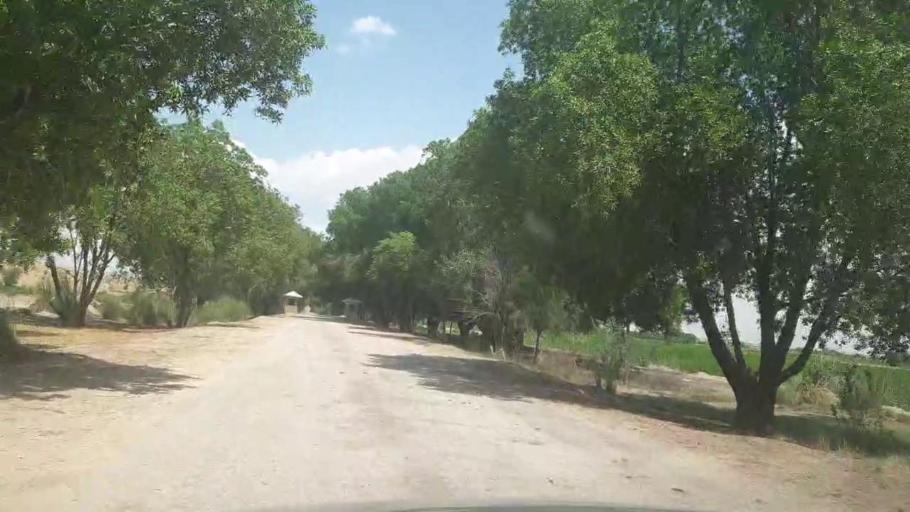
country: PK
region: Sindh
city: Kot Diji
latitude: 27.2196
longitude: 69.0482
